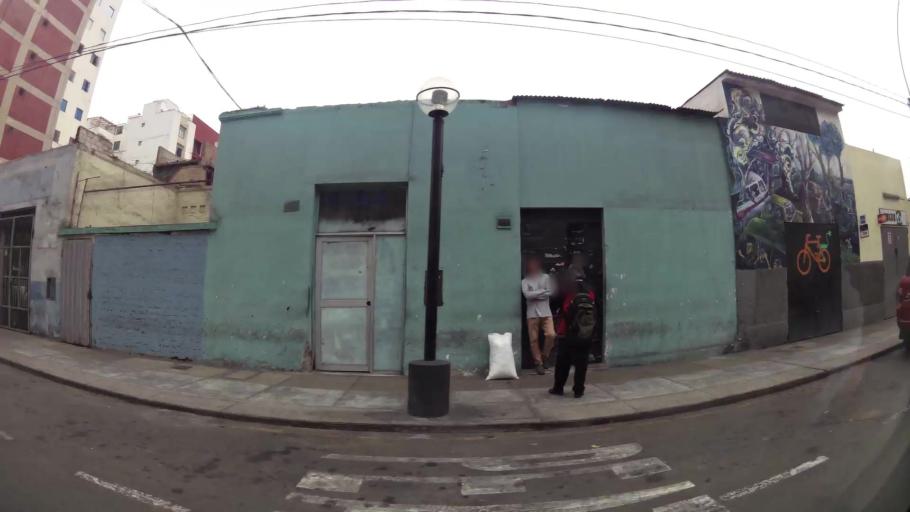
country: PE
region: Lima
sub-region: Lima
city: San Isidro
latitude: -12.1202
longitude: -77.0346
